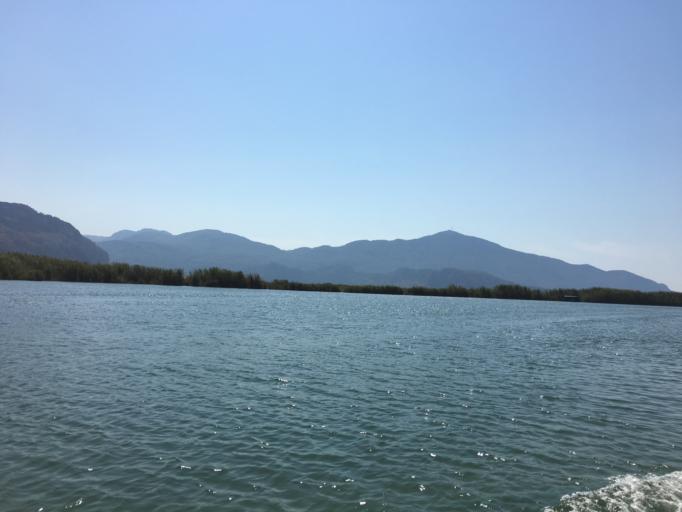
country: TR
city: Dalyan
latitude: 36.8160
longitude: 28.6337
